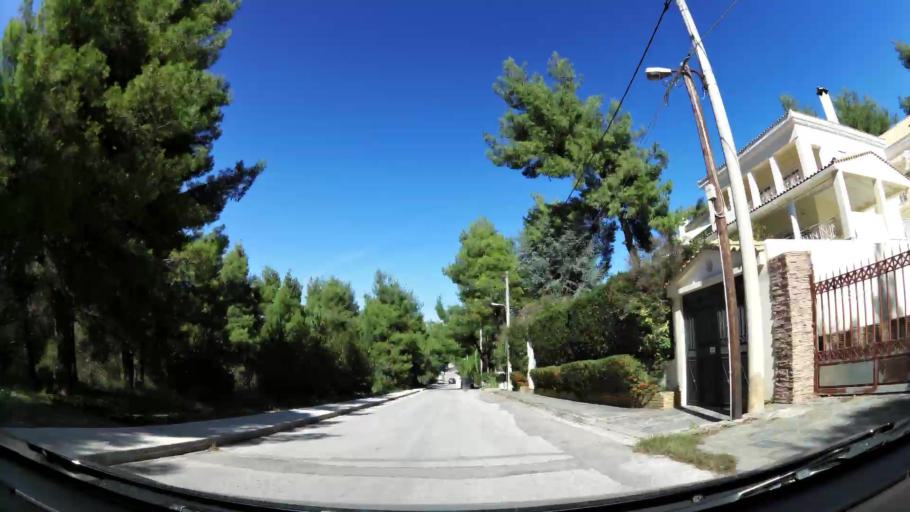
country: GR
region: Attica
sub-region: Nomarchia Anatolikis Attikis
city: Dionysos
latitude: 38.1074
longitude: 23.8718
